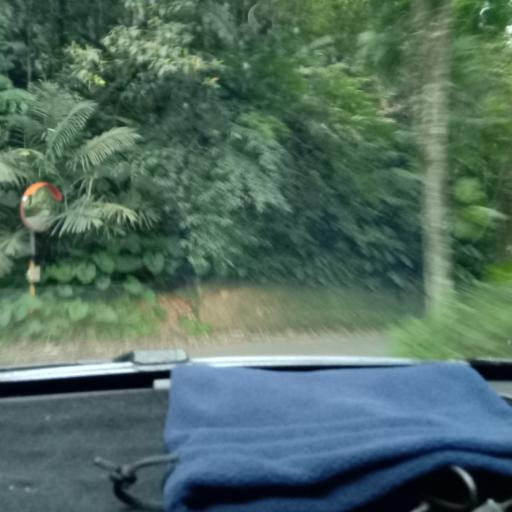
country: TW
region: Taiwan
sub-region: Yilan
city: Yilan
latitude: 24.8111
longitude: 121.7034
